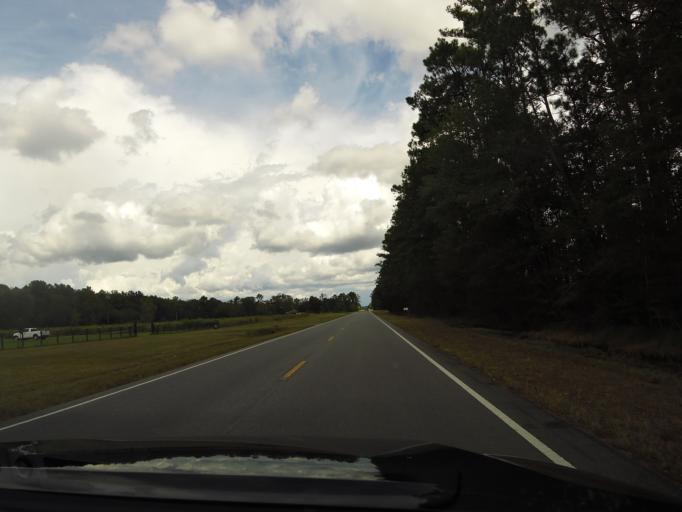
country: US
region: Georgia
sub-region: Brantley County
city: Nahunta
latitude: 31.0733
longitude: -82.0120
